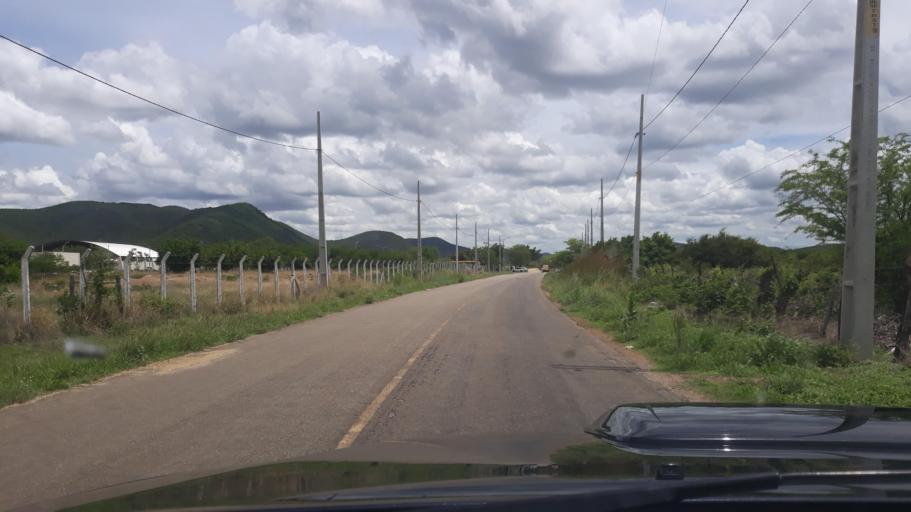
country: BR
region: Bahia
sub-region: Guanambi
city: Guanambi
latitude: -14.3003
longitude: -42.6956
